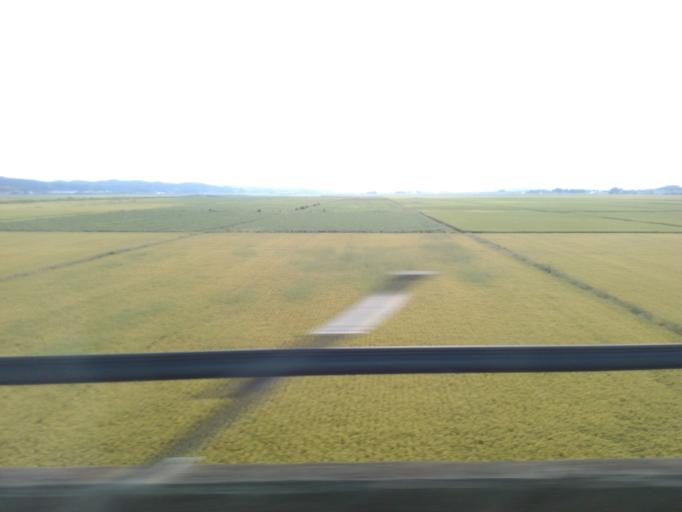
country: JP
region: Iwate
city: Ichinoseki
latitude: 38.7951
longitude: 141.0948
